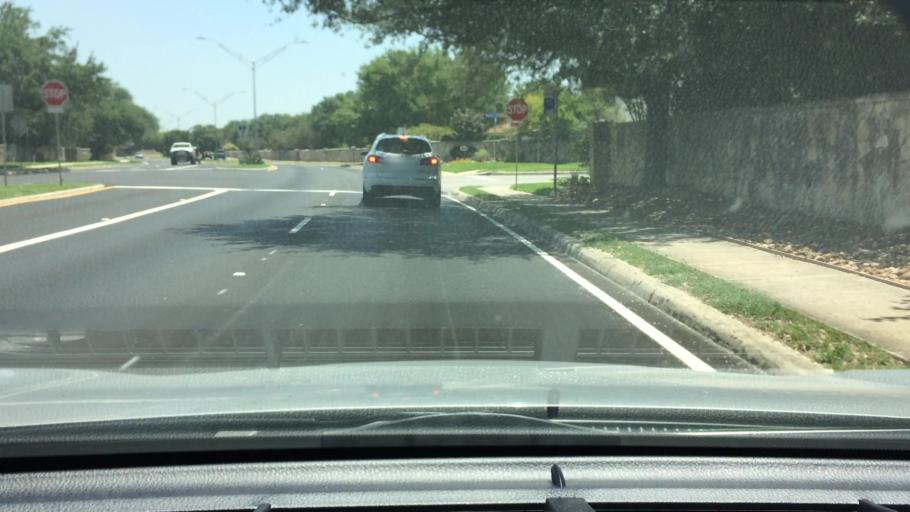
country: US
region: Texas
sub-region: Bexar County
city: Shavano Park
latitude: 29.5586
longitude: -98.5791
